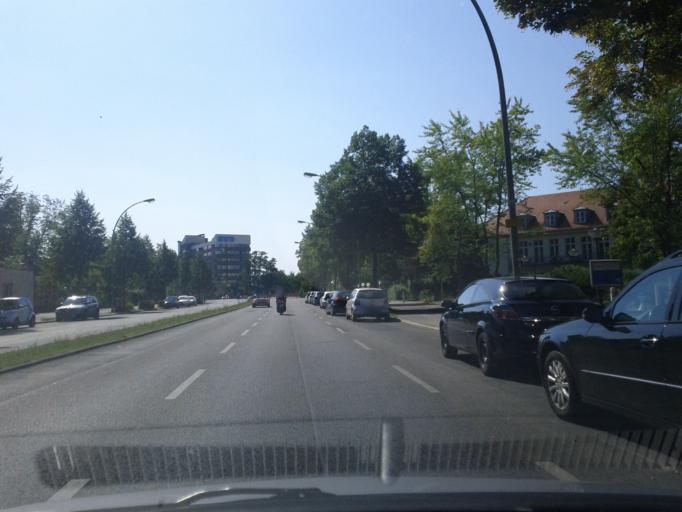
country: DE
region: Berlin
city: Wedding Bezirk
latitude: 52.5402
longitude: 13.3465
